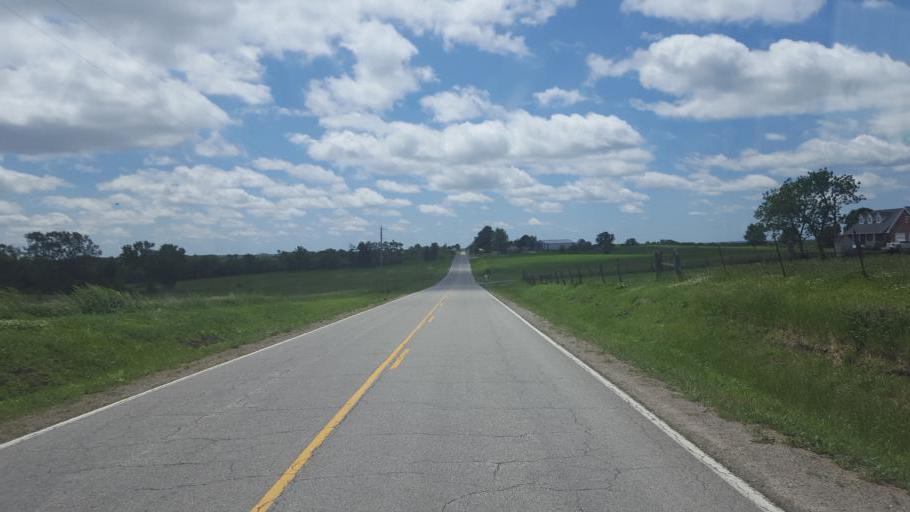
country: US
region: Missouri
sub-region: Harrison County
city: Bethany
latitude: 40.3343
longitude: -94.0163
